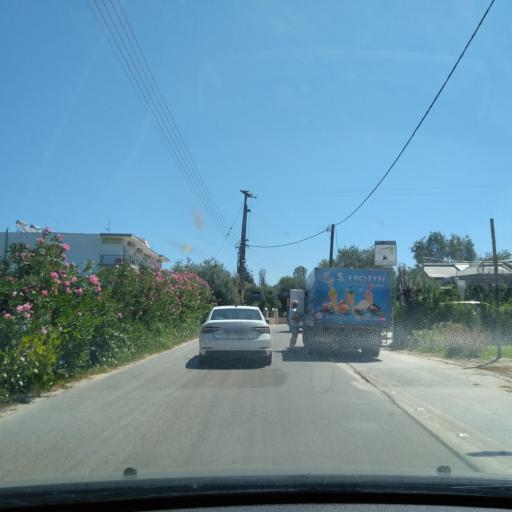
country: GR
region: Central Macedonia
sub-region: Nomos Chalkidikis
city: Neos Marmaras
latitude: 40.1870
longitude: 23.7917
